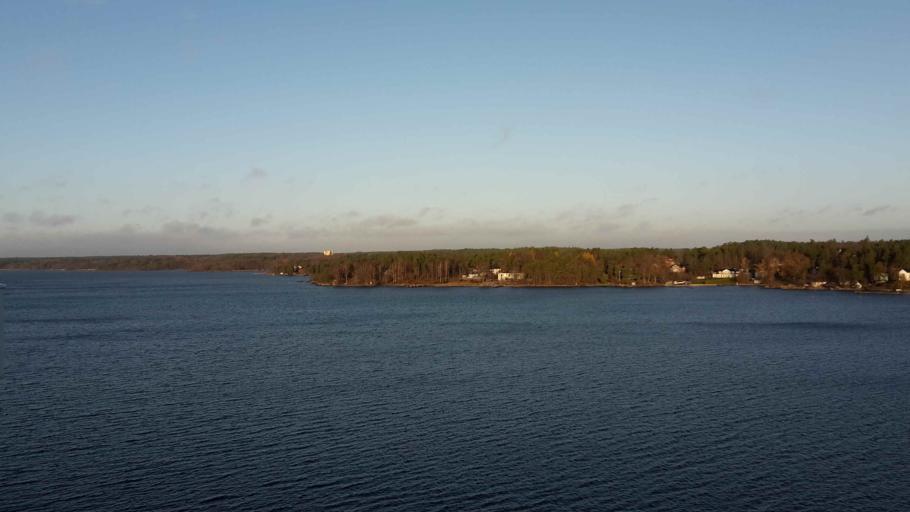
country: SE
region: Stockholm
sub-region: Vaxholms Kommun
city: Vaxholm
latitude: 59.3775
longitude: 18.3279
